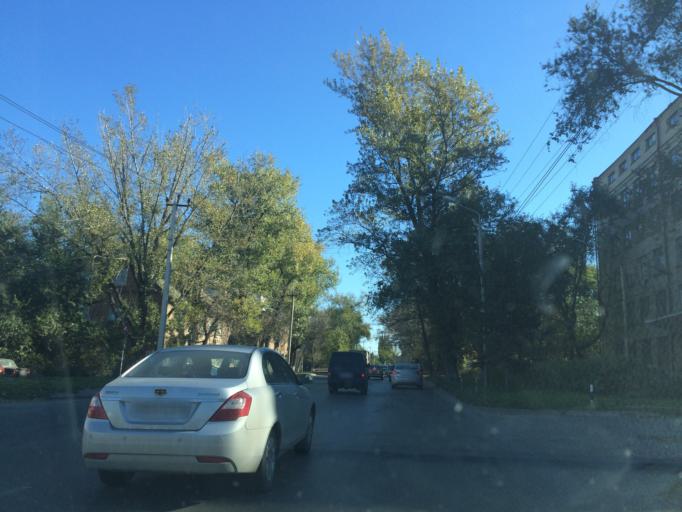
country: RU
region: Rostov
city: Rostov-na-Donu
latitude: 47.2469
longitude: 39.6738
